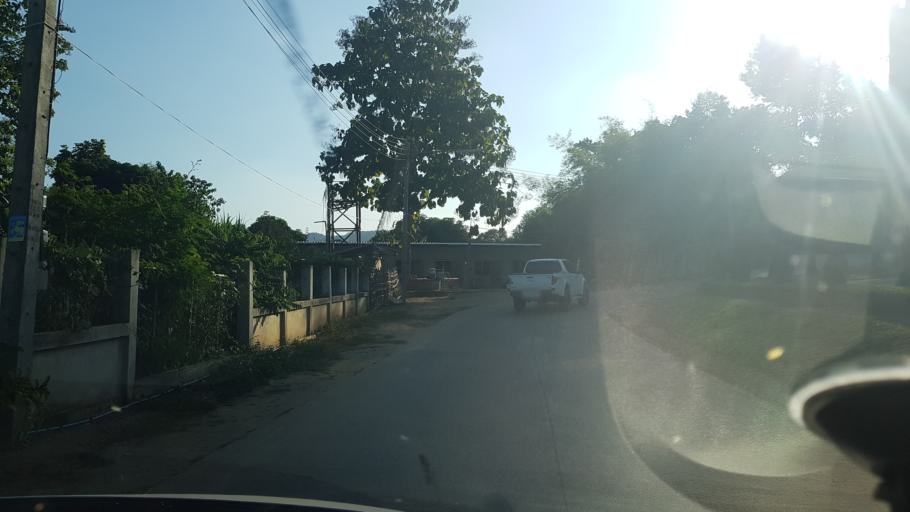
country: TH
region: Chiang Rai
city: Chiang Rai
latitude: 19.9478
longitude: 99.8073
